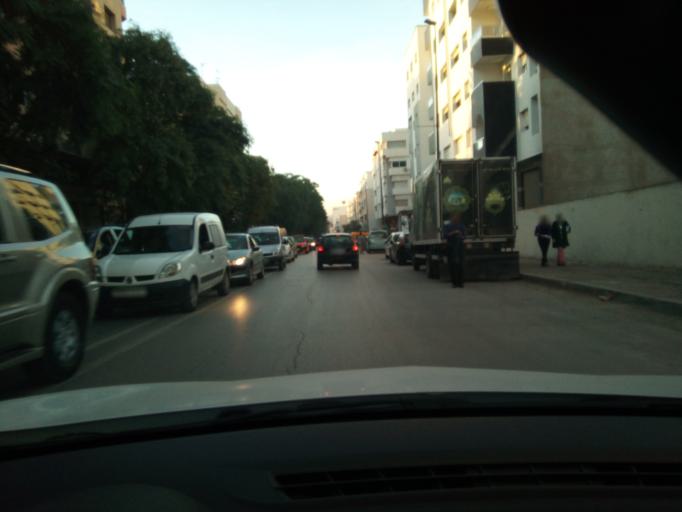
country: MA
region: Fes-Boulemane
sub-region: Fes
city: Fes
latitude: 34.0289
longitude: -4.9923
